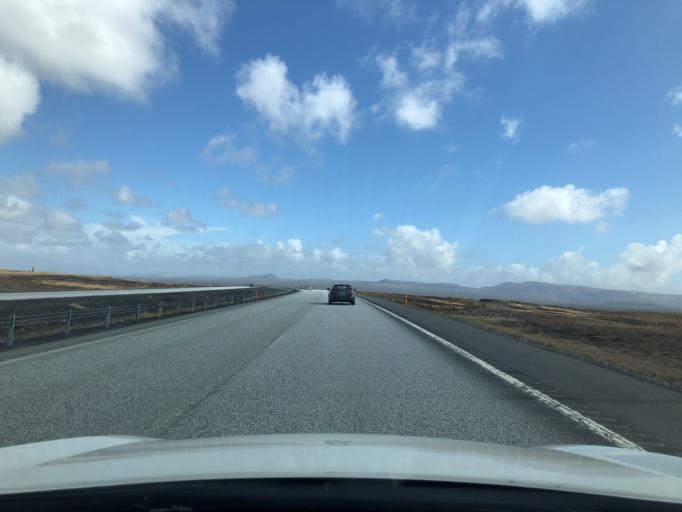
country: IS
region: Southern Peninsula
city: Vogar
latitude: 63.9621
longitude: -22.4555
